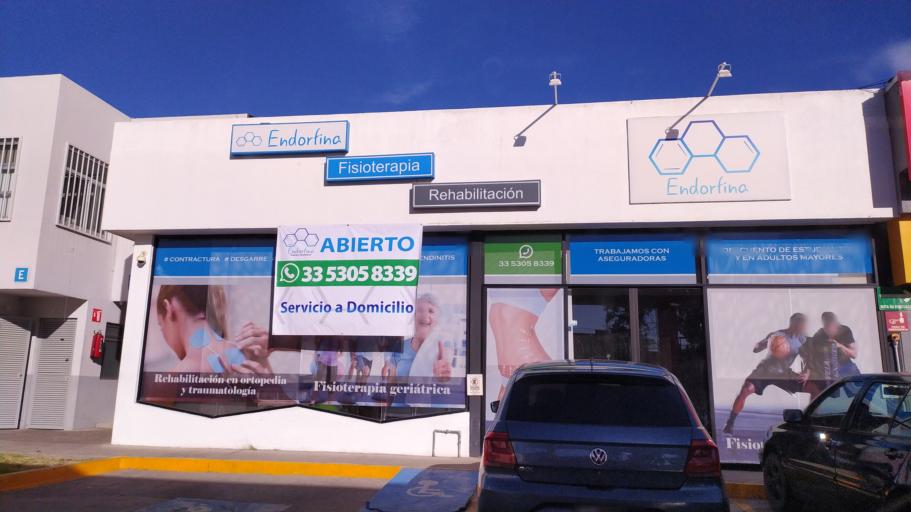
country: MX
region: Jalisco
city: Guadalajara
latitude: 20.6694
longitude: -103.4317
